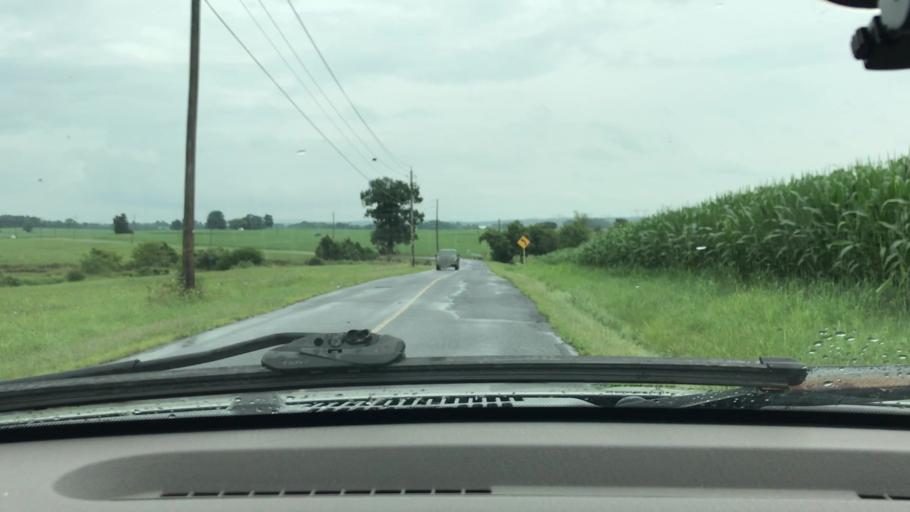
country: US
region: Pennsylvania
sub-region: Lancaster County
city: Elizabethtown
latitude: 40.1934
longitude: -76.6127
